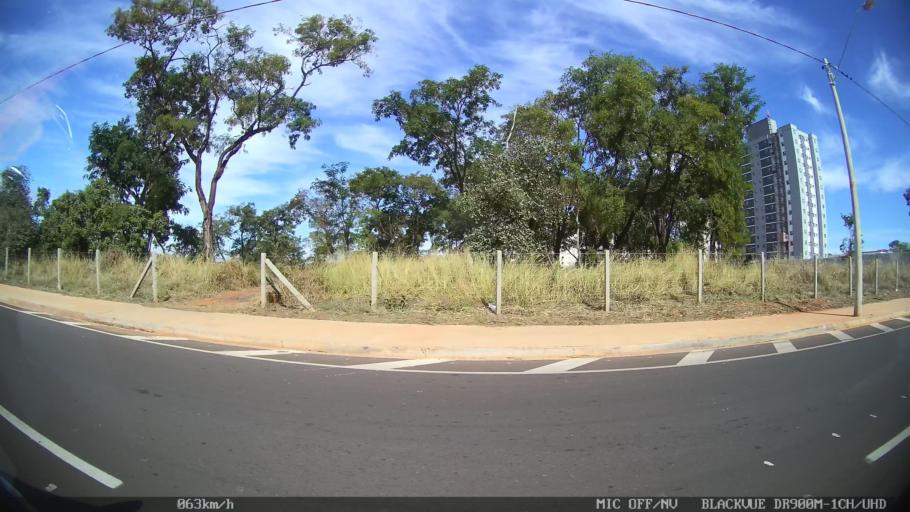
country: BR
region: Sao Paulo
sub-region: Sao Jose Do Rio Preto
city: Sao Jose do Rio Preto
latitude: -20.8250
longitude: -49.3502
